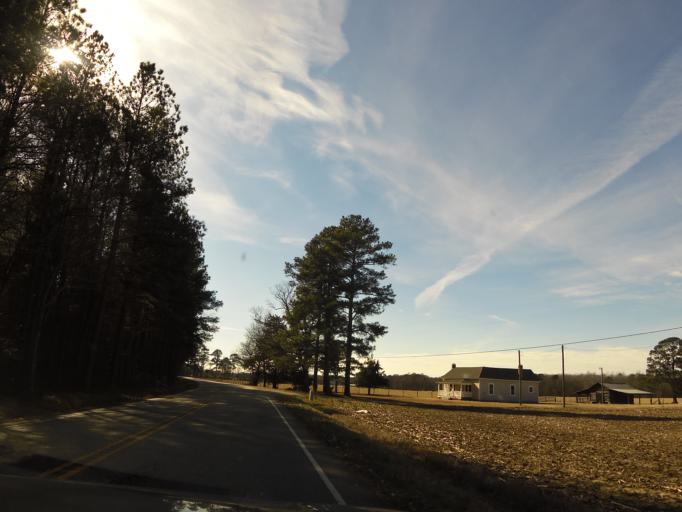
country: US
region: Virginia
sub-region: Isle of Wight County
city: Isle of Wight
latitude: 36.9196
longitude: -76.6942
